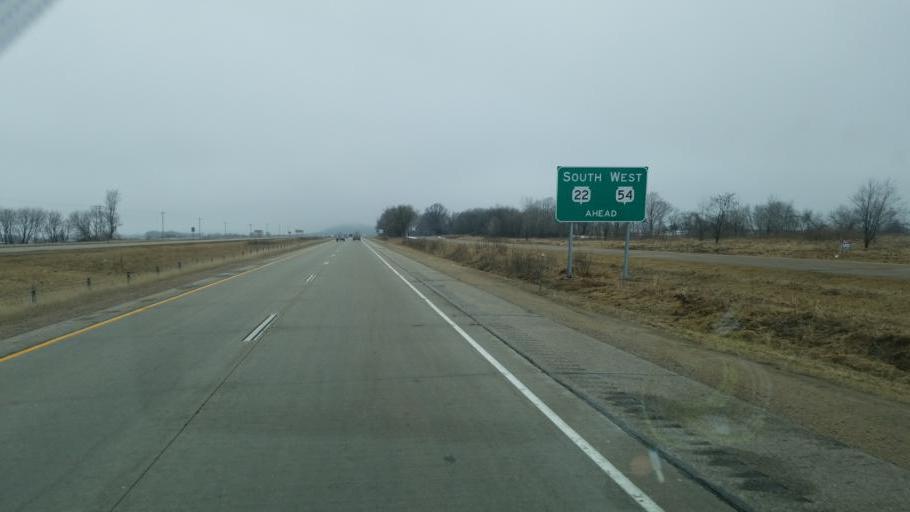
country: US
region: Wisconsin
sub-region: Waupaca County
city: Waupaca
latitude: 44.3295
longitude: -89.0233
